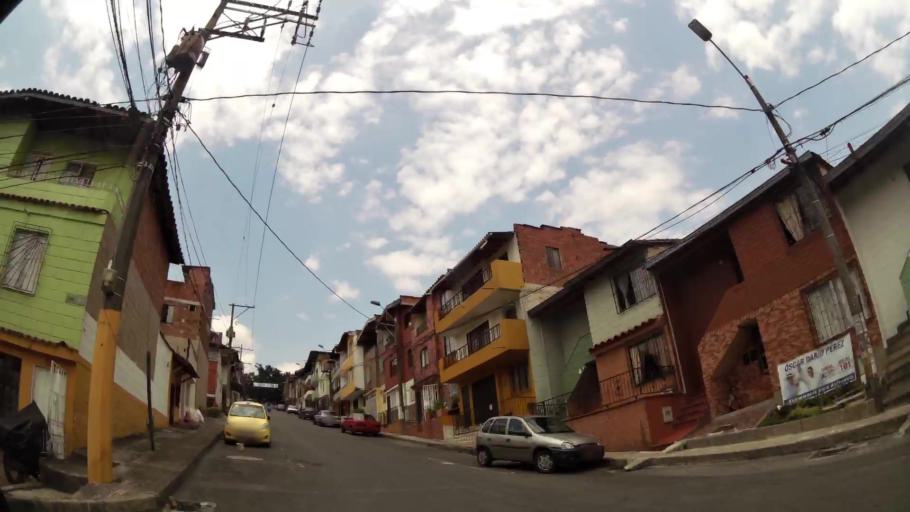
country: CO
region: Antioquia
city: Itagui
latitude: 6.1828
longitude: -75.6030
